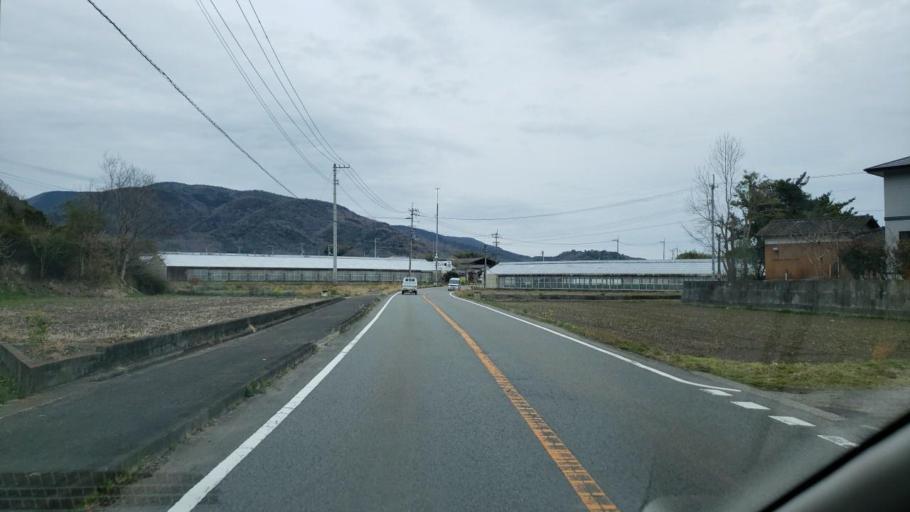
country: JP
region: Tokushima
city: Kamojimacho-jogejima
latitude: 34.1207
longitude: 134.3441
